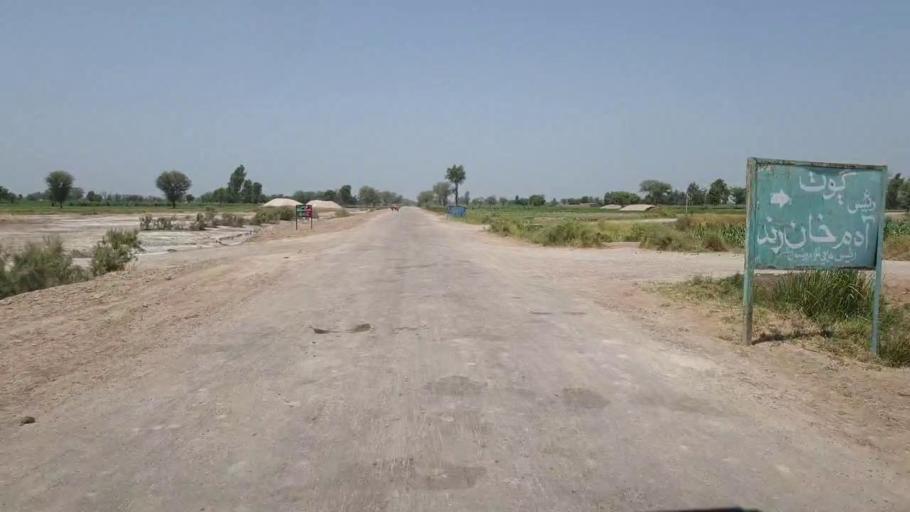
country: PK
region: Sindh
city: Nawabshah
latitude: 26.3563
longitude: 68.4000
